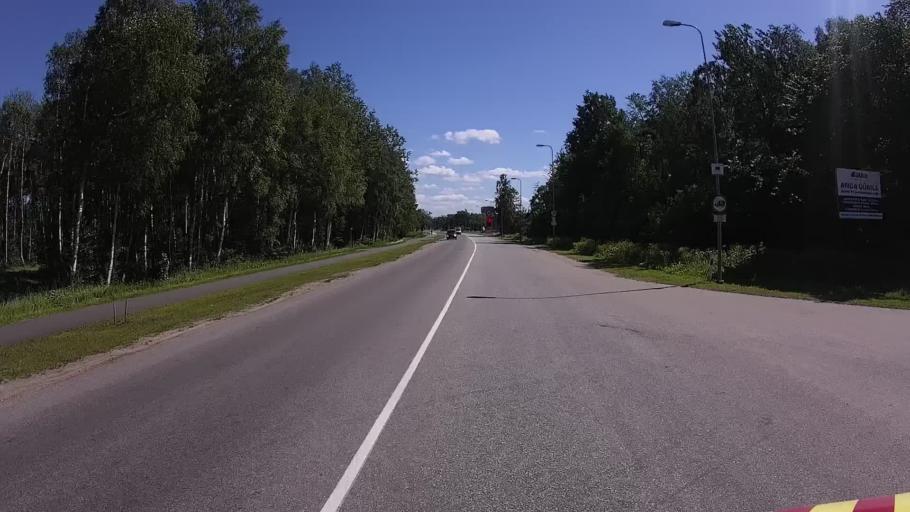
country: EE
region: Ida-Virumaa
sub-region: Kohtla-Jaerve linn
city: Kohtla-Jarve
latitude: 59.4119
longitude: 27.2772
